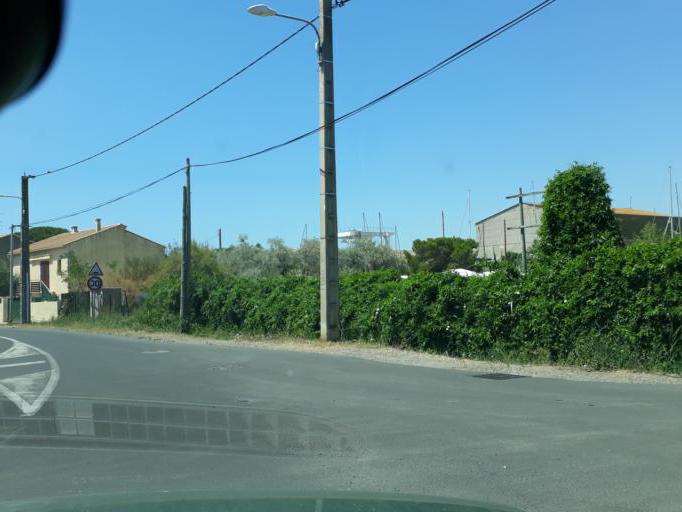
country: FR
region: Languedoc-Roussillon
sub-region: Departement de l'Herault
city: Agde
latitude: 43.2900
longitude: 3.4480
